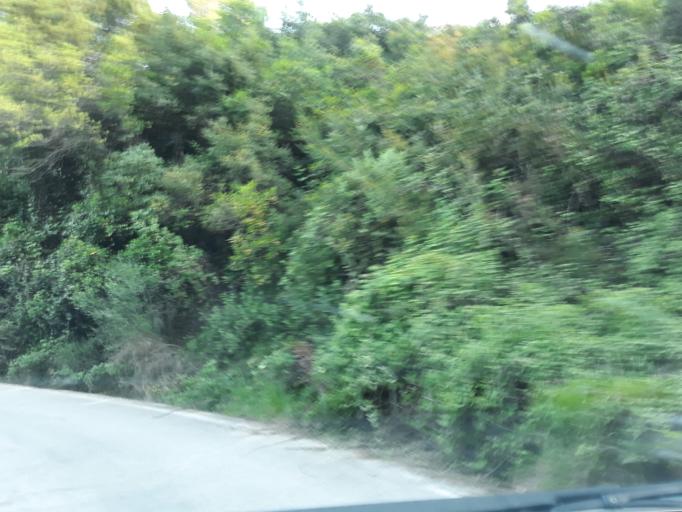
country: GR
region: Attica
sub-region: Nomarchia Anatolikis Attikis
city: Afidnes
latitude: 38.2277
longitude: 23.7883
